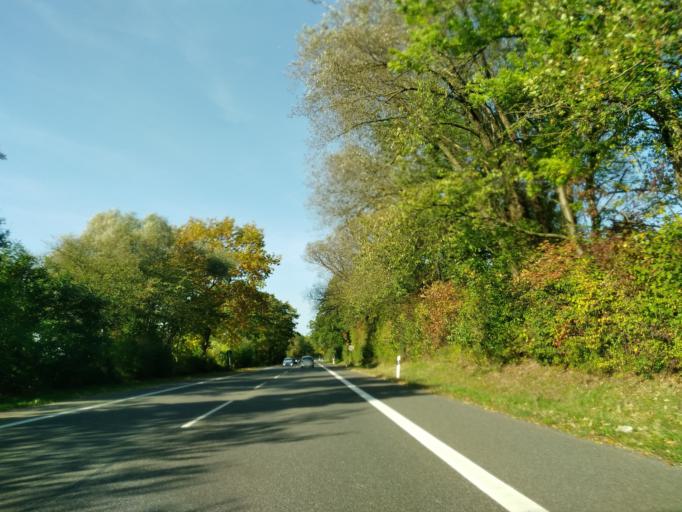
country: DE
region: North Rhine-Westphalia
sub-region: Regierungsbezirk Koln
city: Hennef
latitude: 50.7178
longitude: 7.2788
